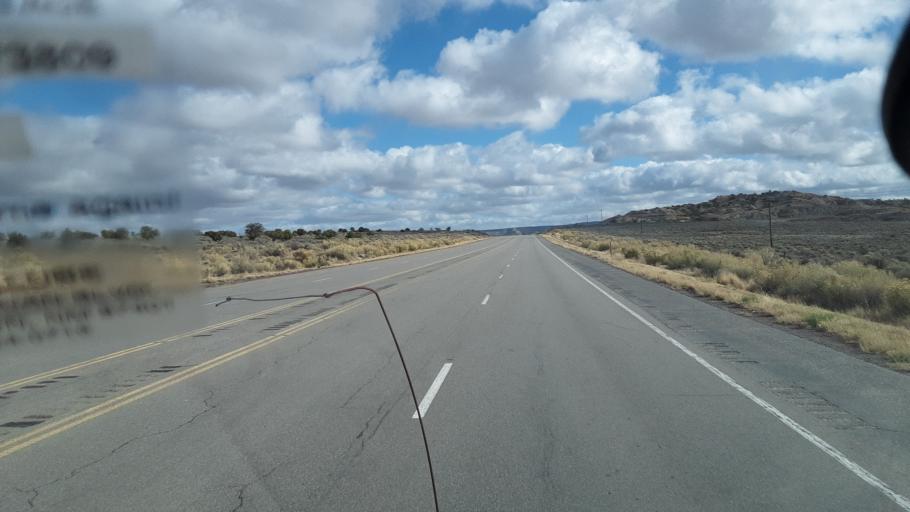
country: US
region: New Mexico
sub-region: San Juan County
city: Bloomfield
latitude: 36.2424
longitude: -107.7034
